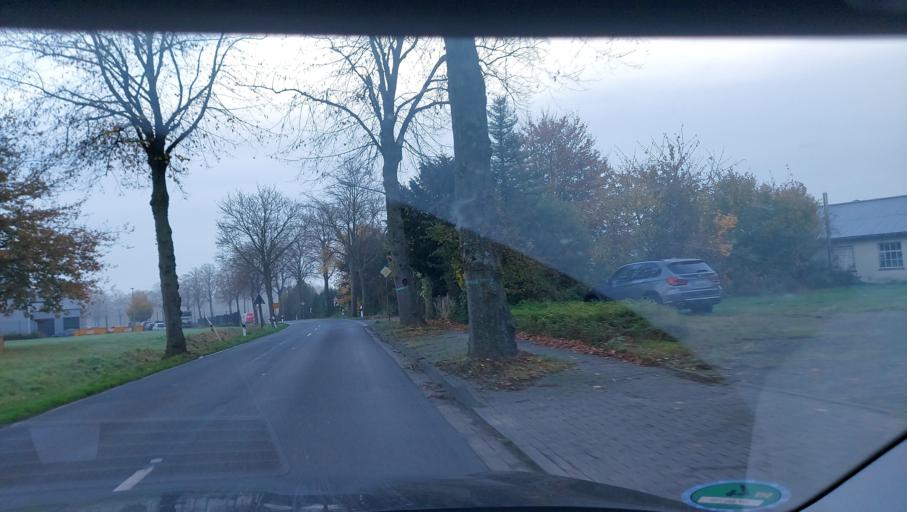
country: DE
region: Lower Saxony
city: Neuenkirchen
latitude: 52.1503
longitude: 8.4315
